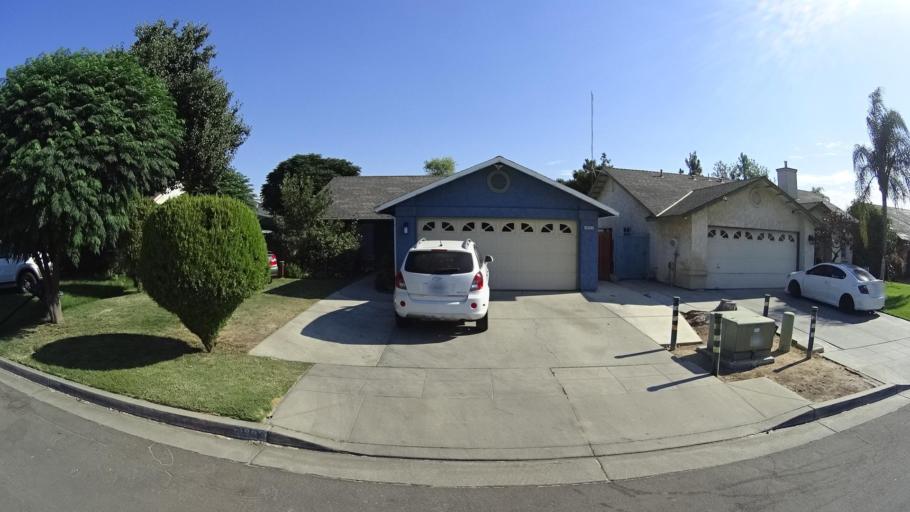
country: US
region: California
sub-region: Fresno County
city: Sunnyside
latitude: 36.7124
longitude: -119.7327
